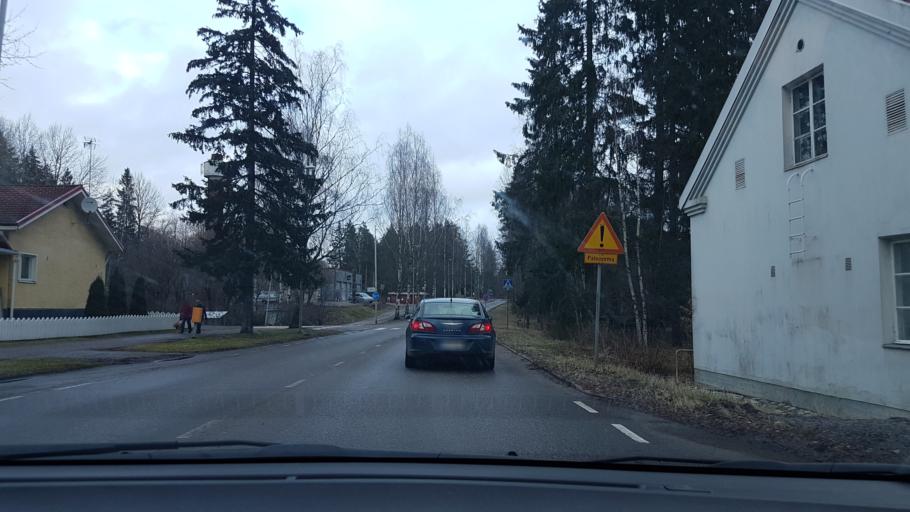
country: FI
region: Uusimaa
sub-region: Helsinki
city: Kerava
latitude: 60.3772
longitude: 25.0817
